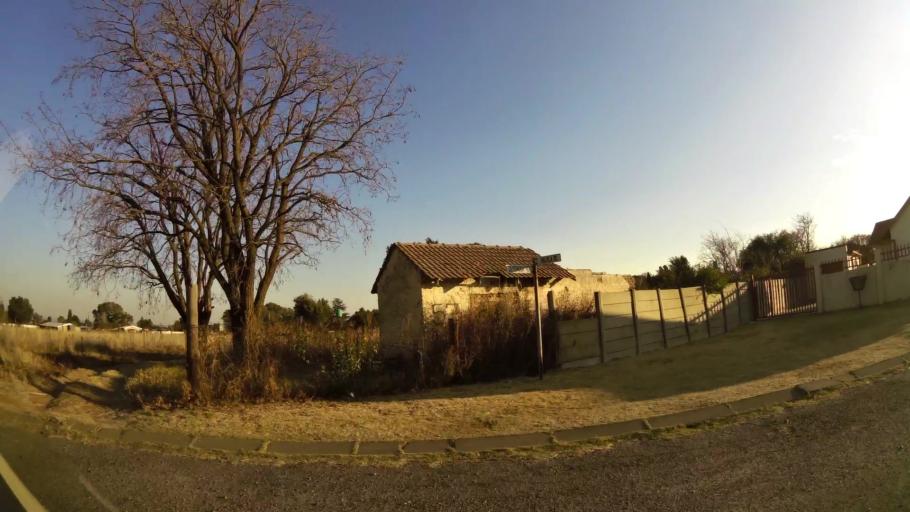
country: ZA
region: Gauteng
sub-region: West Rand District Municipality
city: Randfontein
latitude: -26.2101
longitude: 27.6513
